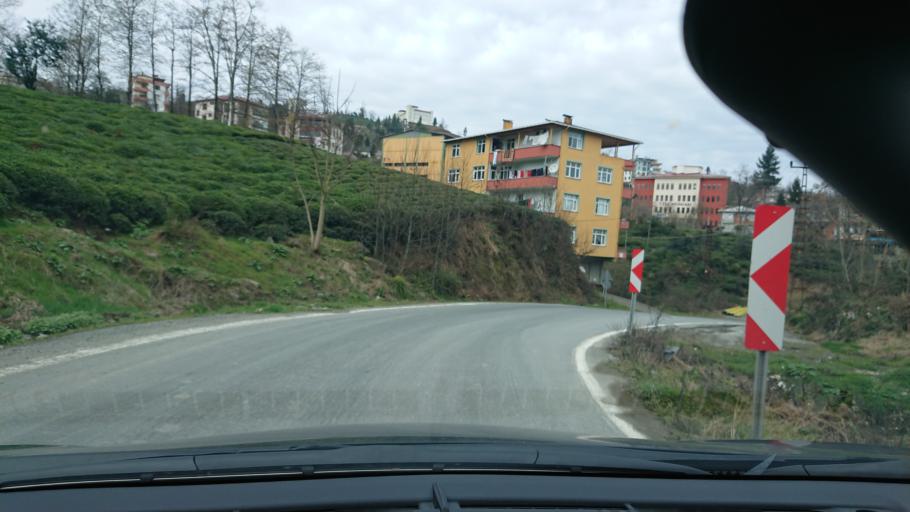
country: TR
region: Rize
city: Rize
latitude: 41.0229
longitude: 40.5022
